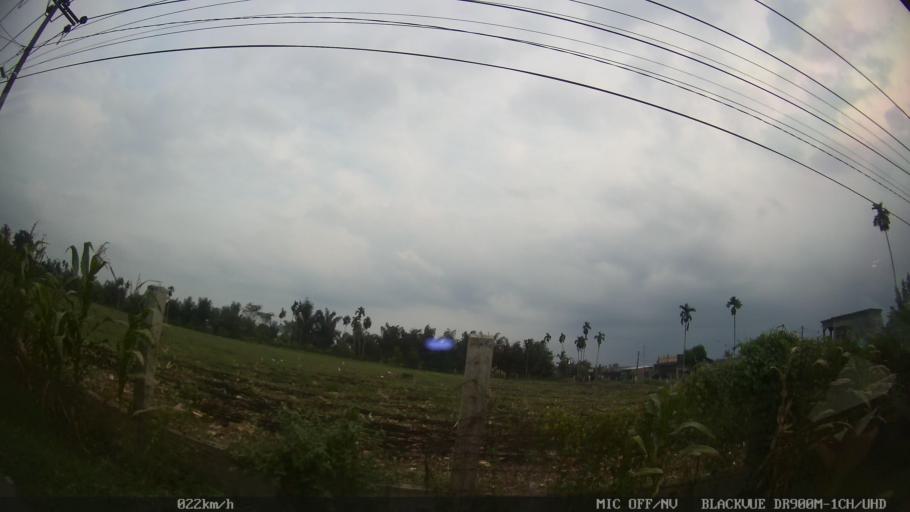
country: ID
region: North Sumatra
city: Sunggal
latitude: 3.5610
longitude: 98.5798
